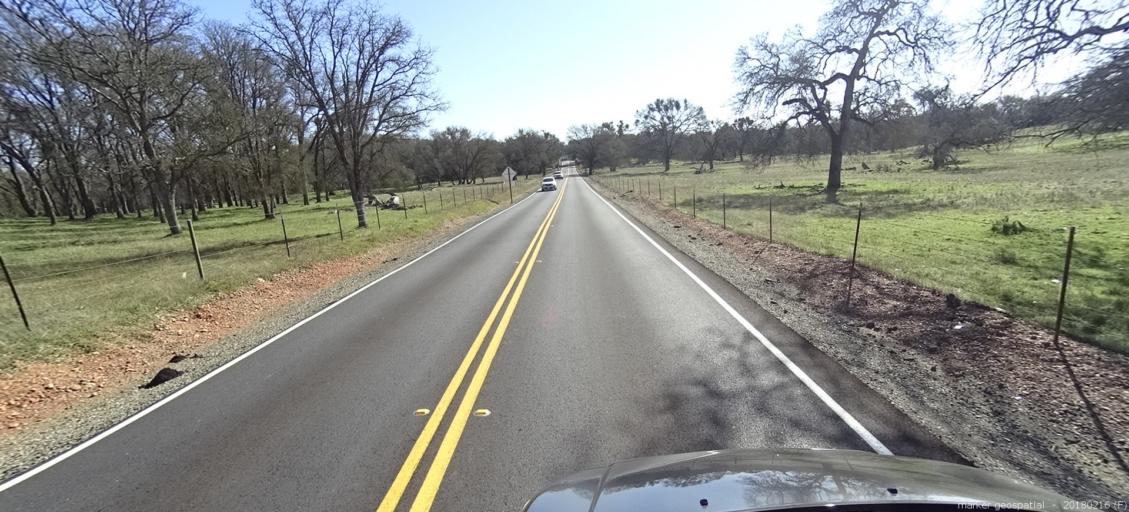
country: US
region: California
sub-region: Sacramento County
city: Rancho Murieta
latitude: 38.5356
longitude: -121.1041
